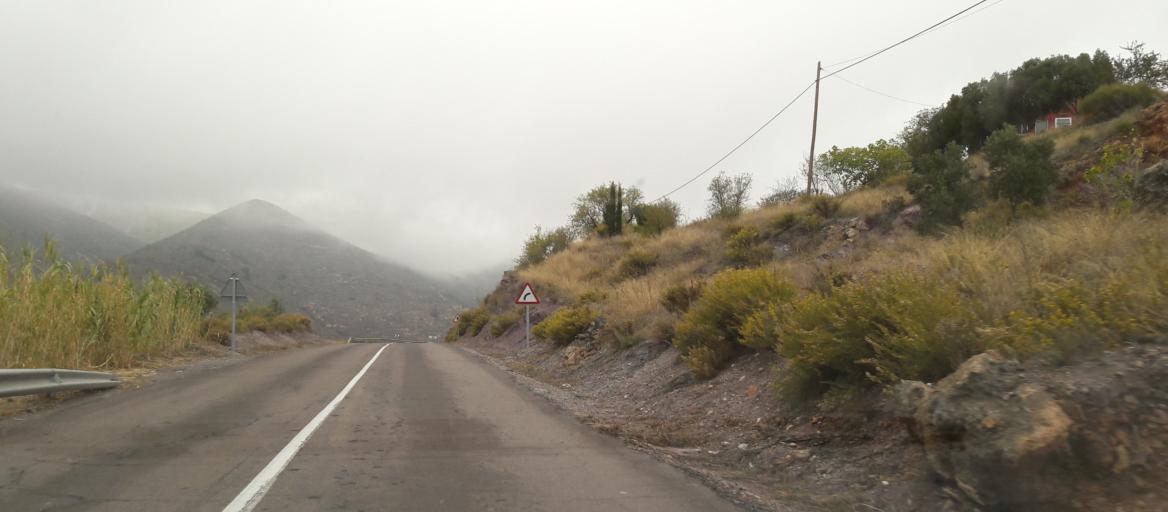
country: ES
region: Andalusia
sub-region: Provincia de Almeria
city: Enix
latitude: 36.8841
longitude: -2.6255
